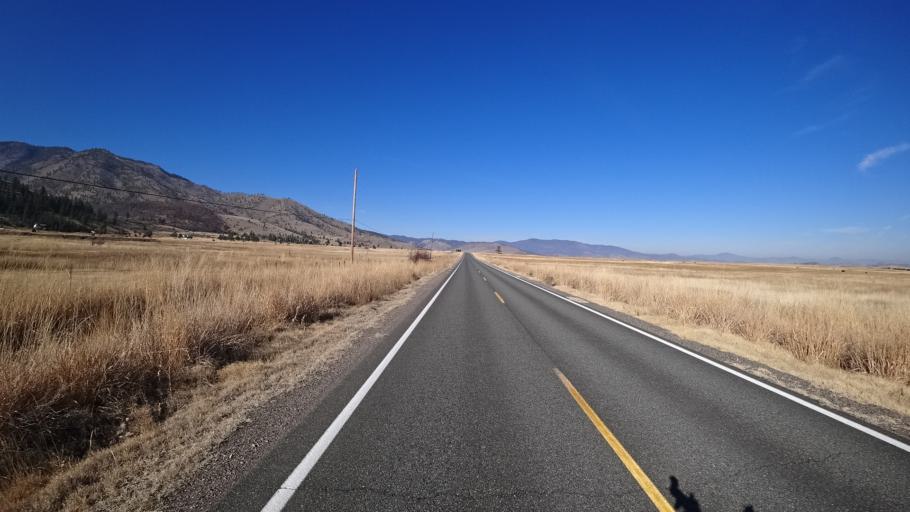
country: US
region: California
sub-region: Siskiyou County
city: Weed
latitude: 41.4716
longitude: -122.4794
